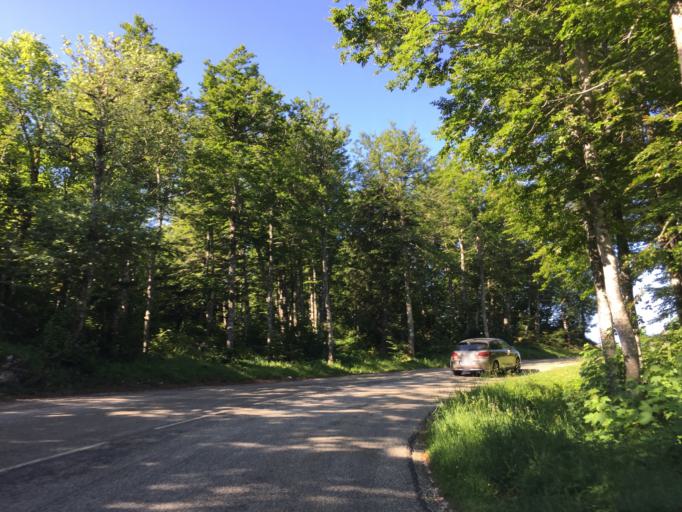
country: FR
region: Rhone-Alpes
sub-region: Departement de la Drome
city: Saint-Jean-en-Royans
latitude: 44.9034
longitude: 5.3353
